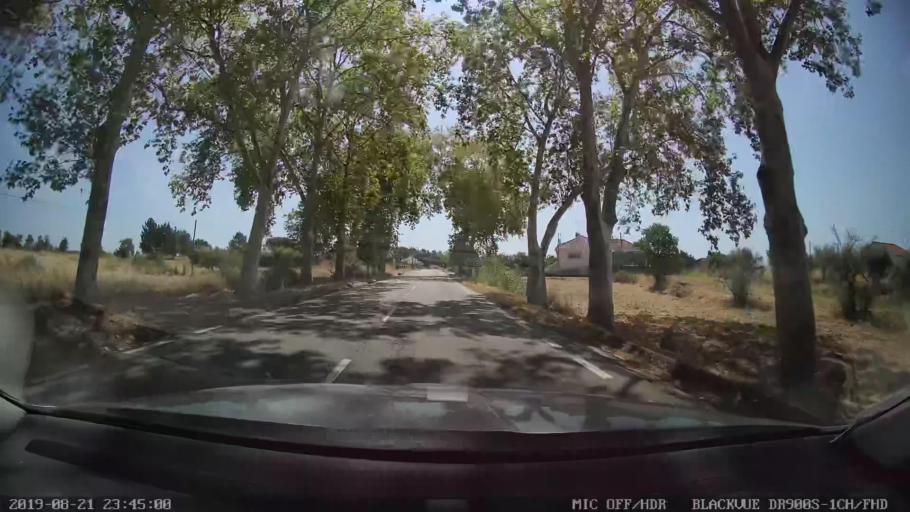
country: PT
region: Castelo Branco
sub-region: Idanha-A-Nova
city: Idanha-a-Nova
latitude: 39.8424
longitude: -7.2698
